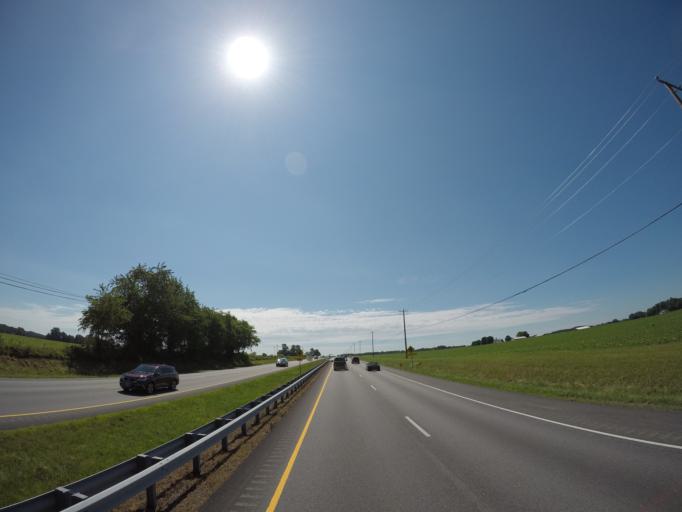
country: US
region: Maryland
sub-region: Queen Anne's County
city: Grasonville
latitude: 38.9743
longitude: -76.1264
